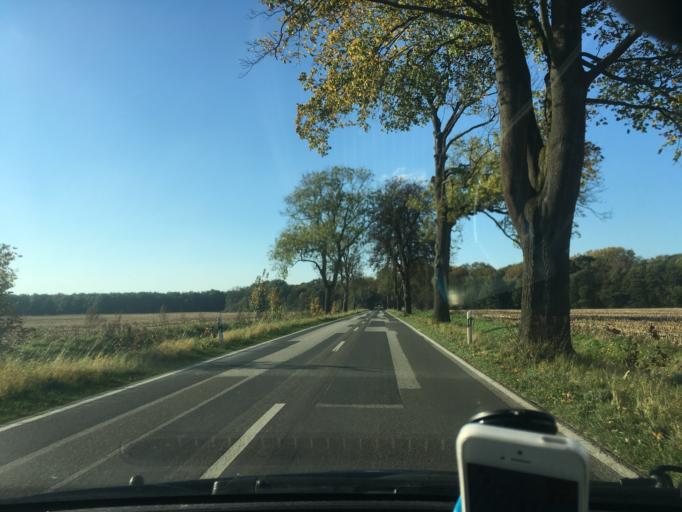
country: DE
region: Mecklenburg-Vorpommern
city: Zarrentin
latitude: 53.5233
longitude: 10.9900
